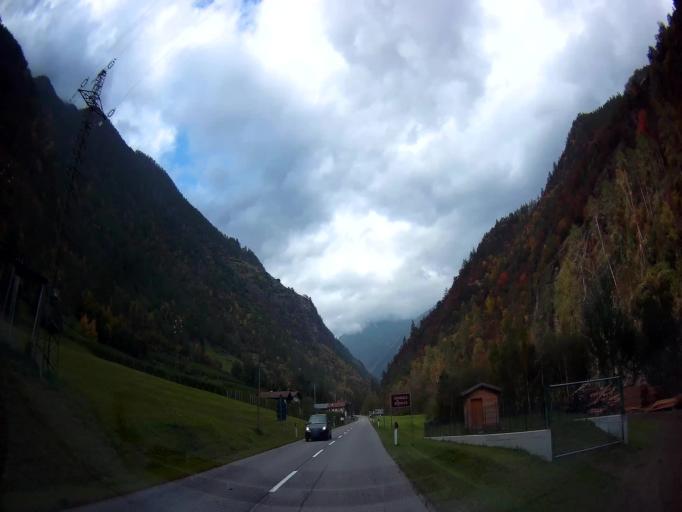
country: IT
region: Trentino-Alto Adige
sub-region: Bolzano
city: Certosa
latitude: 46.6699
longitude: 10.9450
